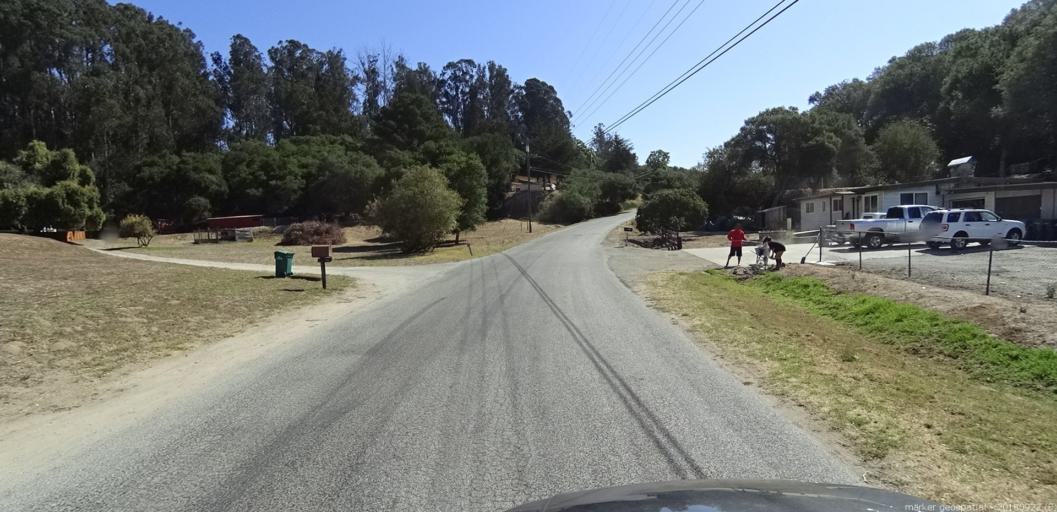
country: US
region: California
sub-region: Monterey County
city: Prunedale
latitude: 36.8109
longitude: -121.6338
